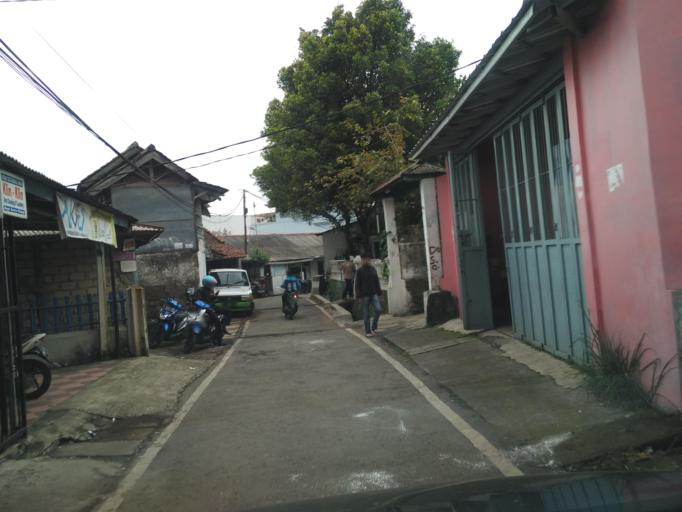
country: ID
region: West Java
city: Caringin
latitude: -6.7295
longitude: 107.0384
